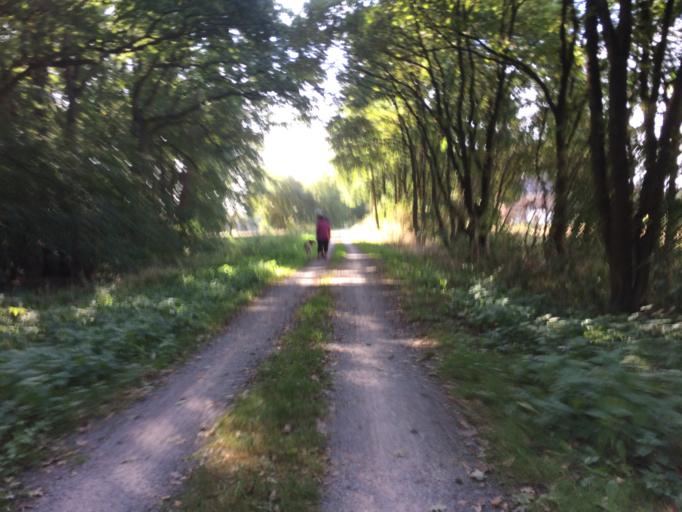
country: DE
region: North Rhine-Westphalia
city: Marl
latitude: 51.7016
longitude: 7.0747
